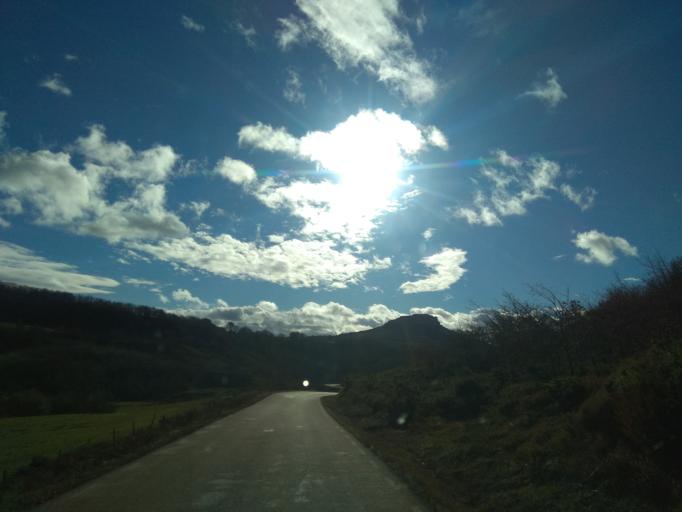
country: ES
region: Cantabria
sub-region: Provincia de Cantabria
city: San Martin de Elines
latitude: 42.9350
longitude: -3.8345
